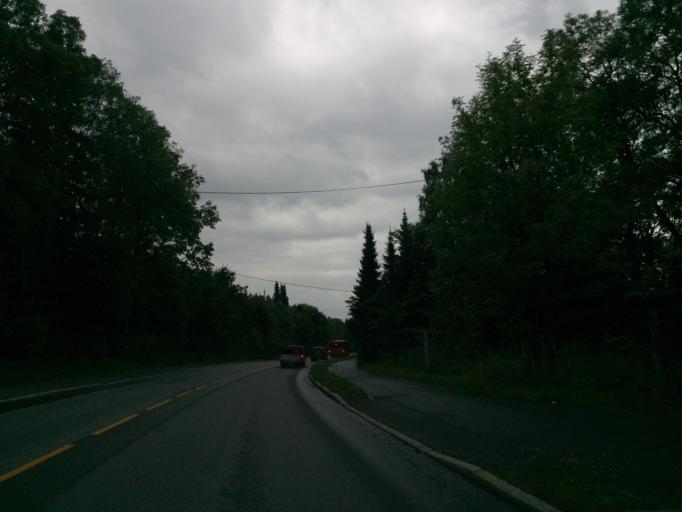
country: NO
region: Oslo
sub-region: Oslo
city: Sjolyststranda
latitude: 59.9442
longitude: 10.6804
